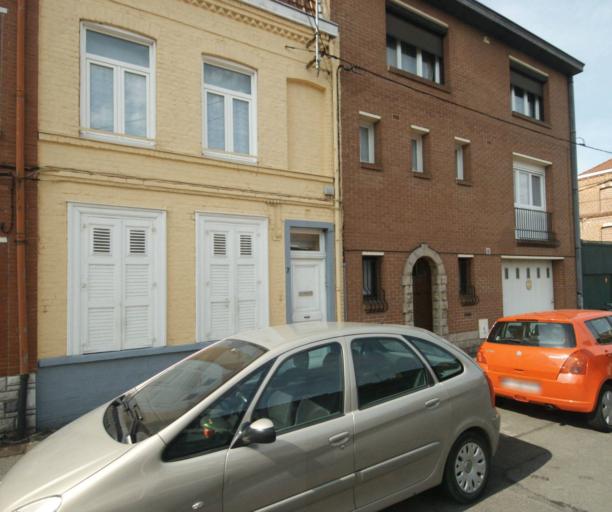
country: FR
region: Nord-Pas-de-Calais
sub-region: Departement du Nord
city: Faches-Thumesnil
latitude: 50.6076
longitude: 3.0649
